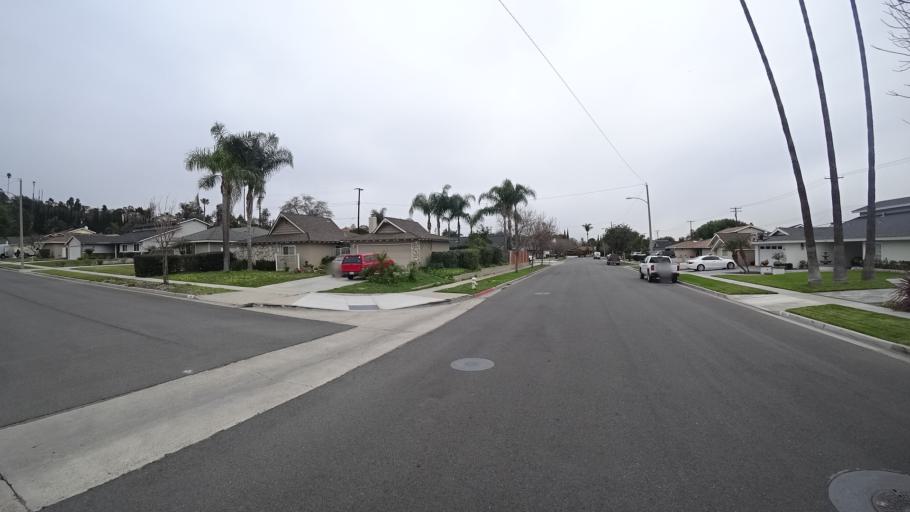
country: US
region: California
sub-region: Orange County
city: Yorba Linda
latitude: 33.8535
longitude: -117.7967
